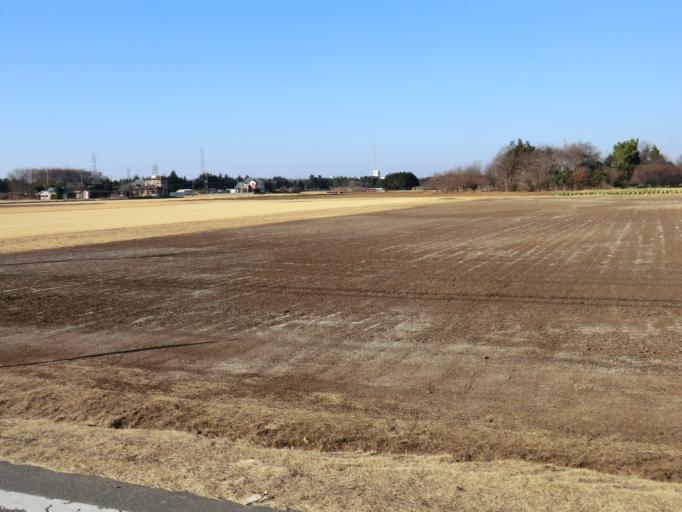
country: JP
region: Ibaraki
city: Tsukuba
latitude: 36.1642
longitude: 140.0356
